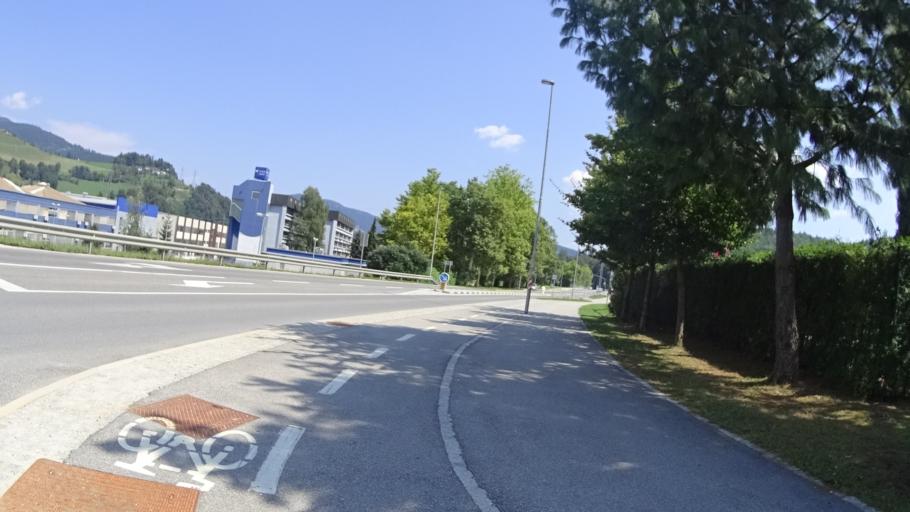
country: SI
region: Ravne na Koroskem
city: Ravne na Koroskem
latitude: 46.5439
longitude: 14.9473
